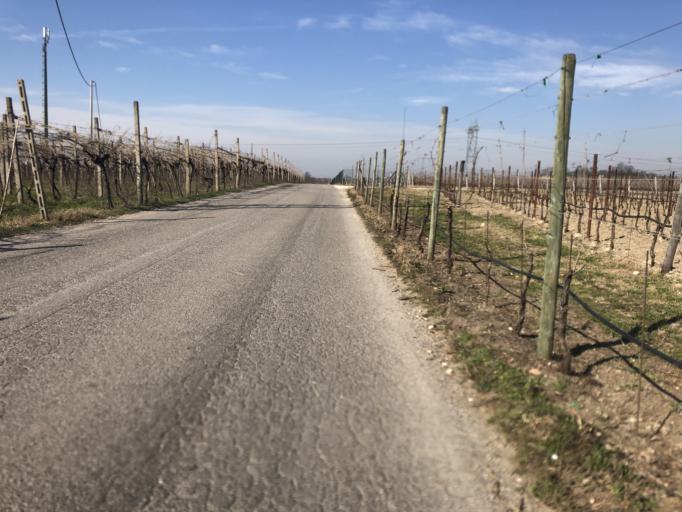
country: IT
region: Veneto
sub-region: Provincia di Verona
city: San Giorgio in Salici
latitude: 45.4171
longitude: 10.8144
